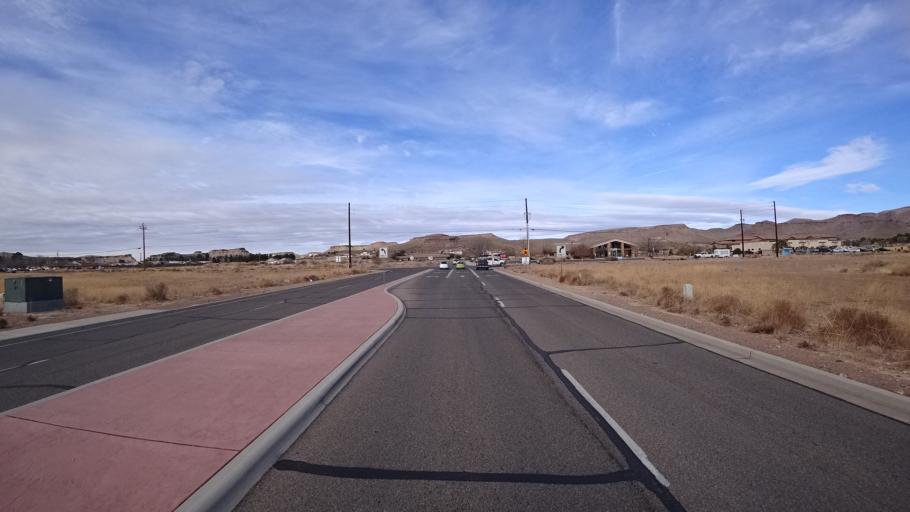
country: US
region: Arizona
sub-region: Mohave County
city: Kingman
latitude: 35.2249
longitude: -114.0393
